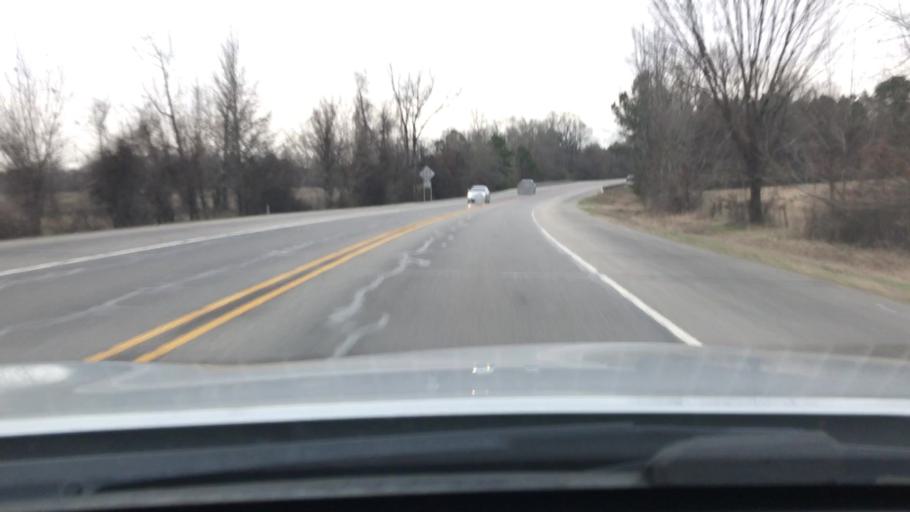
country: US
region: Arkansas
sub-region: Hempstead County
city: Hope
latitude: 33.6859
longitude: -93.5775
